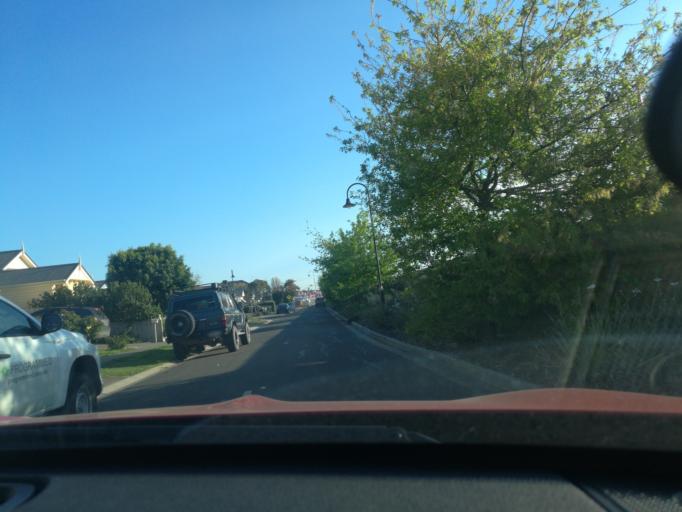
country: AU
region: Victoria
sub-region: Wyndham
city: Williams Landing
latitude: -37.8768
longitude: 144.7484
